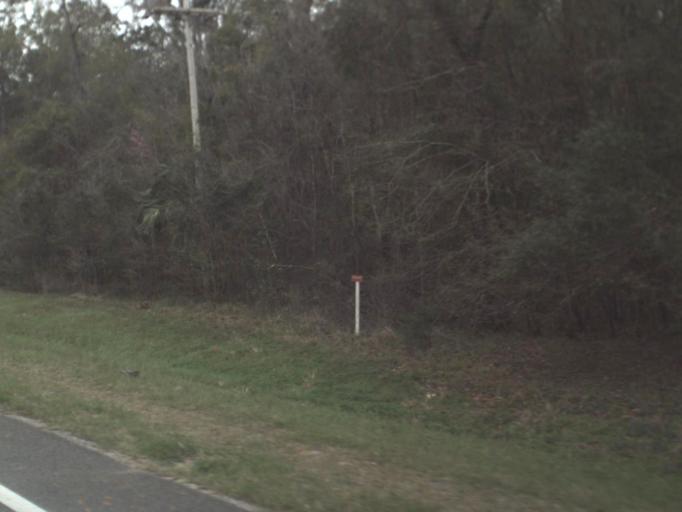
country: US
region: Florida
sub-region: Wakulla County
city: Crawfordville
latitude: 30.1517
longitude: -84.2738
